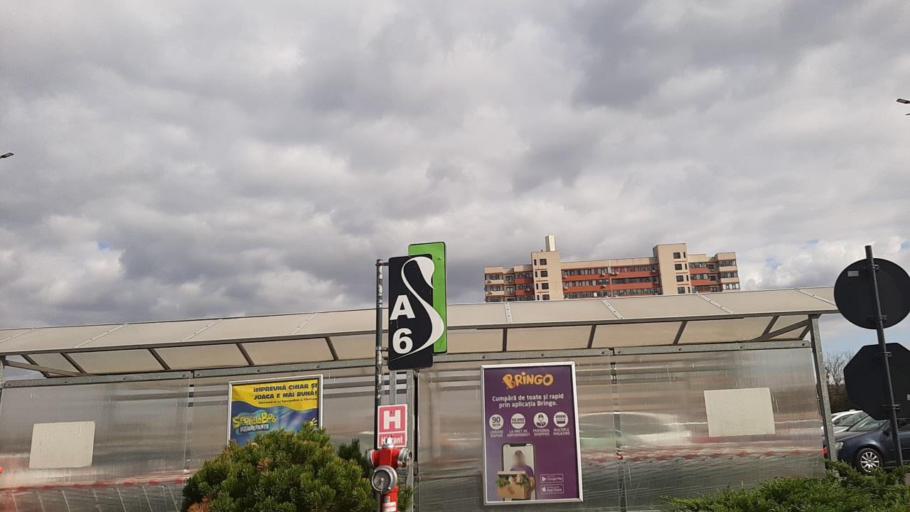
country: RO
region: Galati
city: Galati
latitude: 45.4524
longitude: 28.0319
